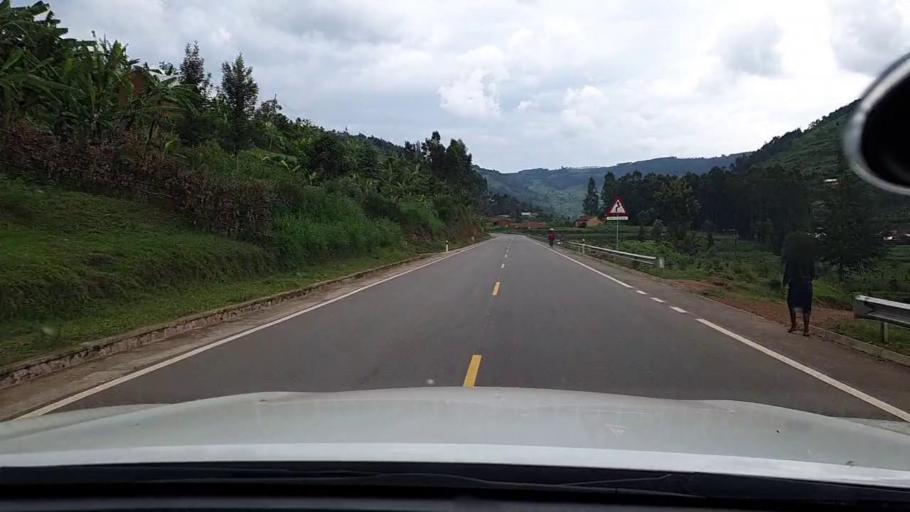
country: RW
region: Northern Province
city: Byumba
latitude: -1.6310
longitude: 29.9275
